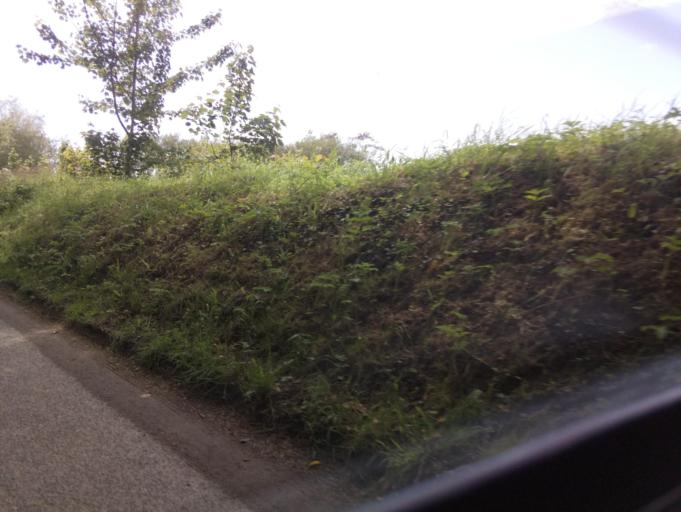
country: GB
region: England
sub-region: Devon
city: South Brent
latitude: 50.3648
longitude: -3.8185
